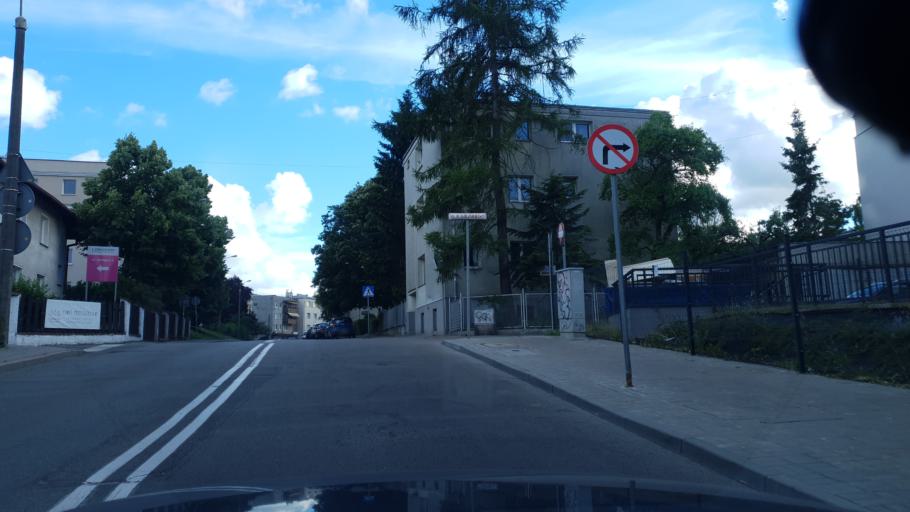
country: PL
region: Pomeranian Voivodeship
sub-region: Gdynia
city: Gdynia
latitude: 54.5055
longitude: 18.5430
